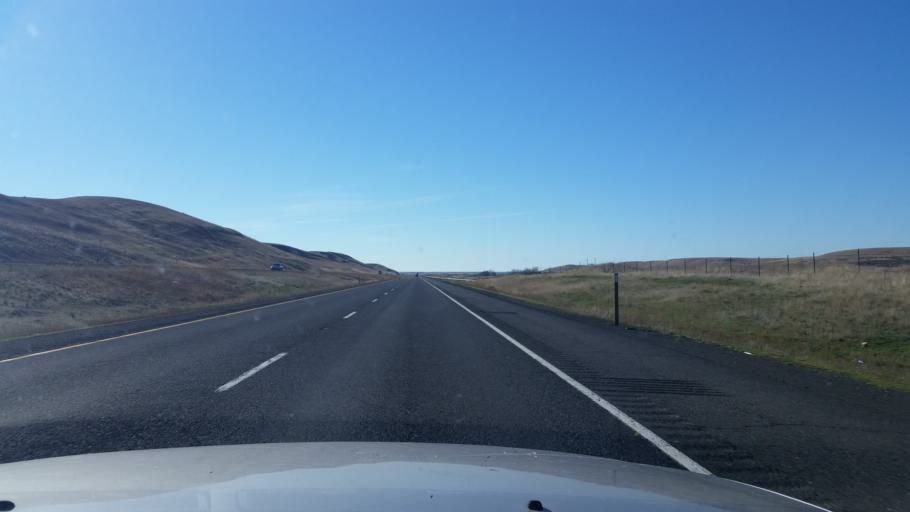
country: US
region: Washington
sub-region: Spokane County
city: Medical Lake
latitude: 47.3646
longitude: -117.8854
